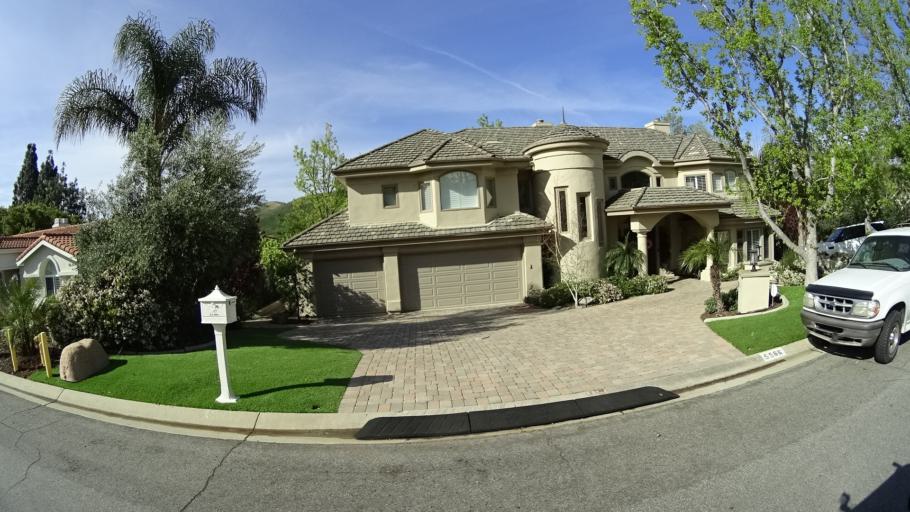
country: US
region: California
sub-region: Ventura County
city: Oak Park
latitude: 34.1911
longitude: -118.7917
